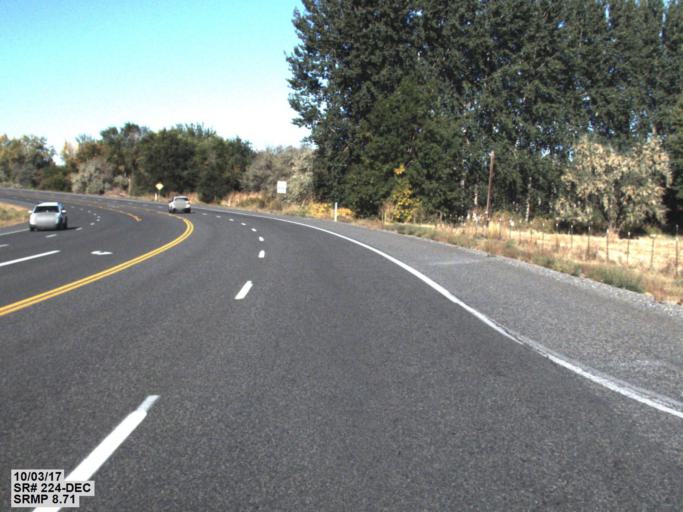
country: US
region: Washington
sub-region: Benton County
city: West Richland
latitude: 46.2979
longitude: -119.3272
